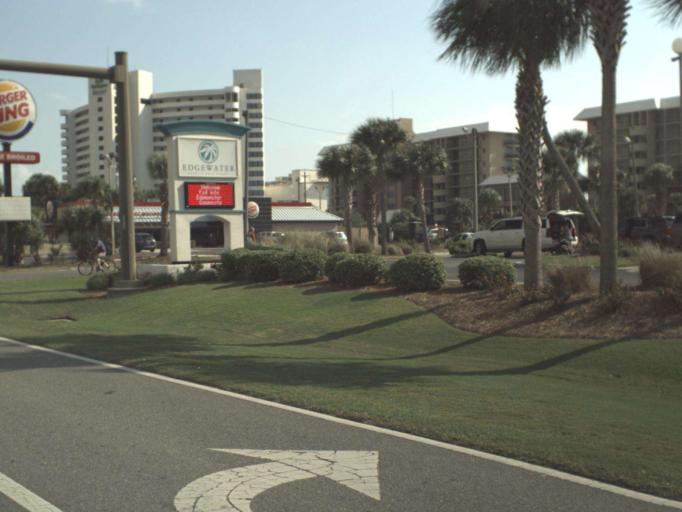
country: US
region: Florida
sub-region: Bay County
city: Panama City Beach
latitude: 30.1851
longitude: -85.8193
